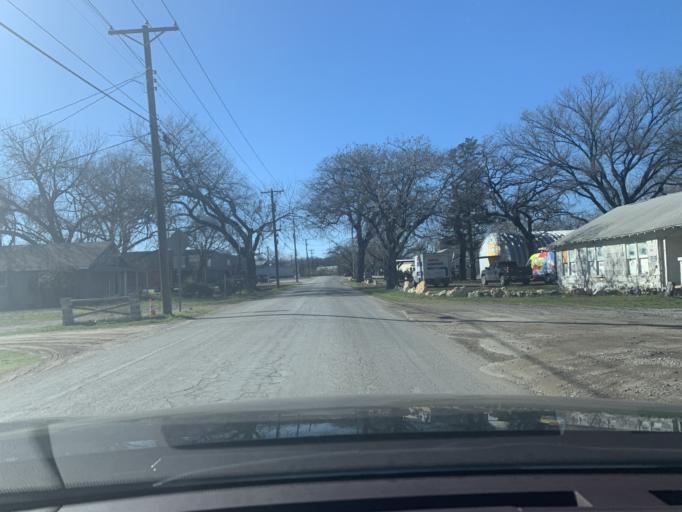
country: US
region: Texas
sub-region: Tarrant County
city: Haltom City
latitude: 32.7766
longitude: -97.2745
